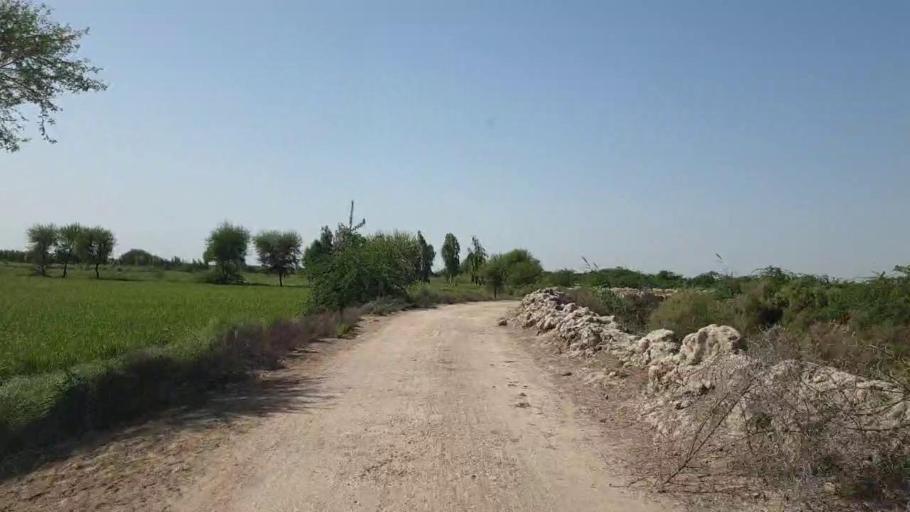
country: PK
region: Sindh
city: Tando Bago
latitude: 24.7062
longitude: 69.0519
